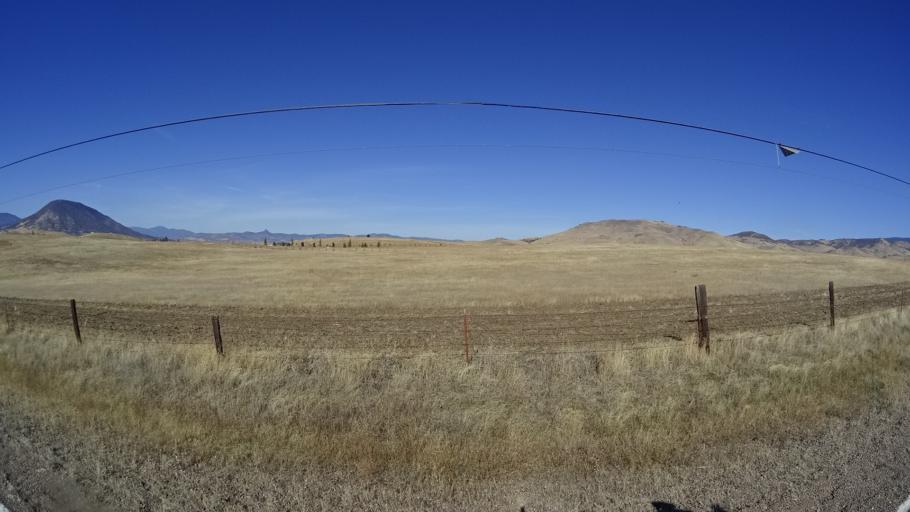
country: US
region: California
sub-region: Siskiyou County
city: Montague
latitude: 41.8070
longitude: -122.4294
